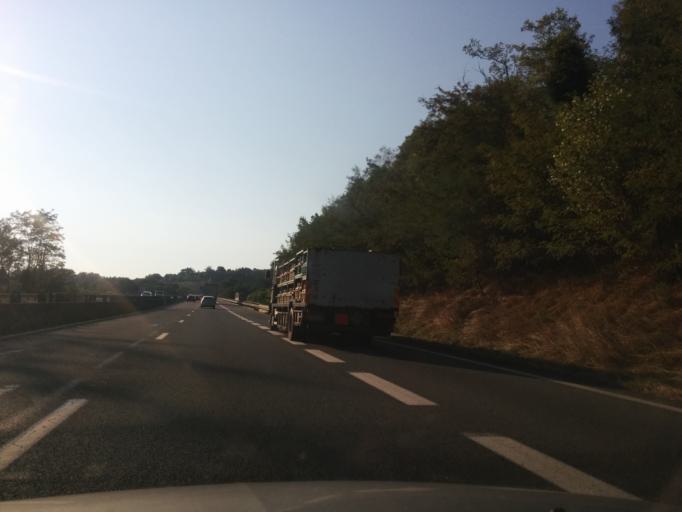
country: FR
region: Rhone-Alpes
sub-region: Departement de l'Isere
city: Saint-Jean-de-Moirans
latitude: 45.3414
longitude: 5.5729
